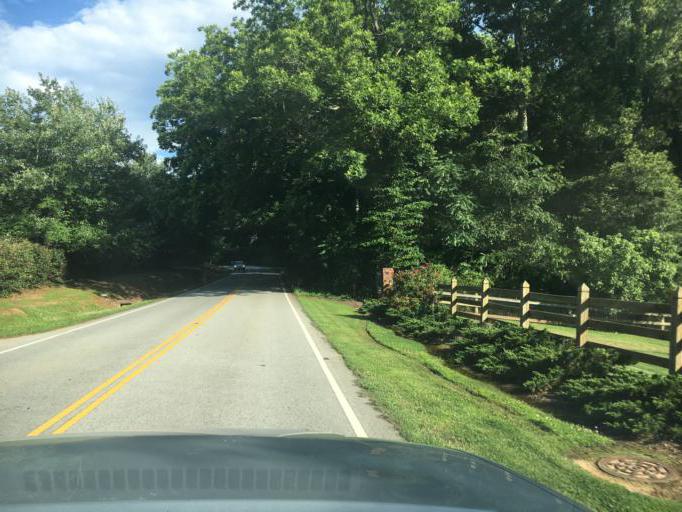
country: US
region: South Carolina
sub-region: Greenville County
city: Simpsonville
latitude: 34.7712
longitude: -82.2650
